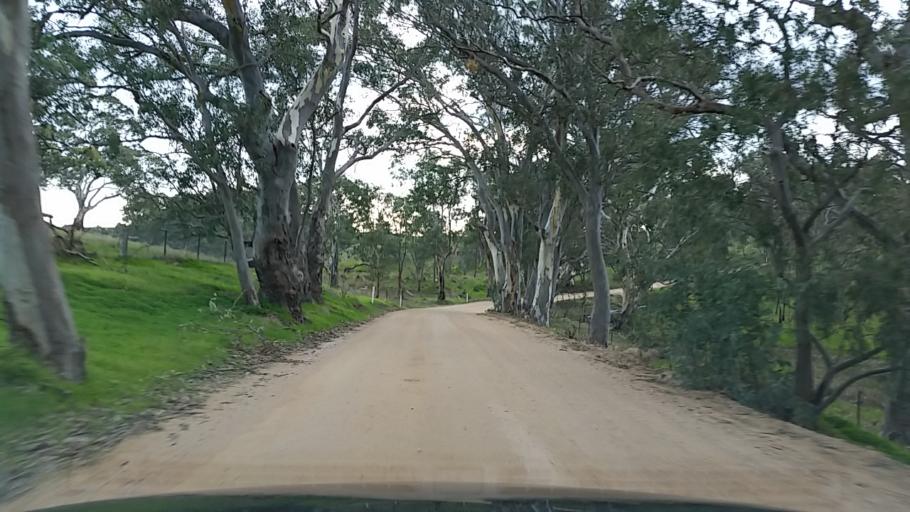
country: AU
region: South Australia
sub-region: Mount Barker
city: Nairne
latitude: -34.9664
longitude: 139.0246
